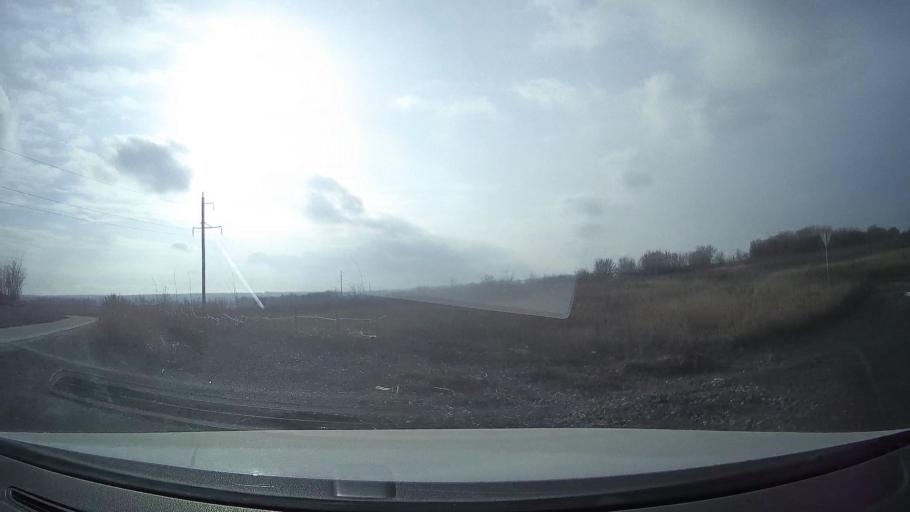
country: RU
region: Rostov
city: Grushevskaya
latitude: 47.4579
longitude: 39.8760
